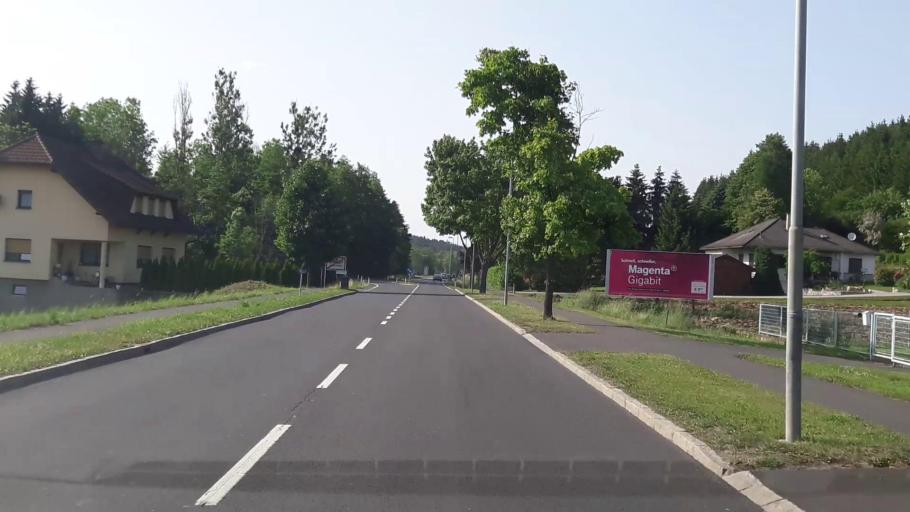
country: AT
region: Burgenland
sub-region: Politischer Bezirk Gussing
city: Ollersdorf im Burgenland
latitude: 47.1897
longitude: 16.1633
